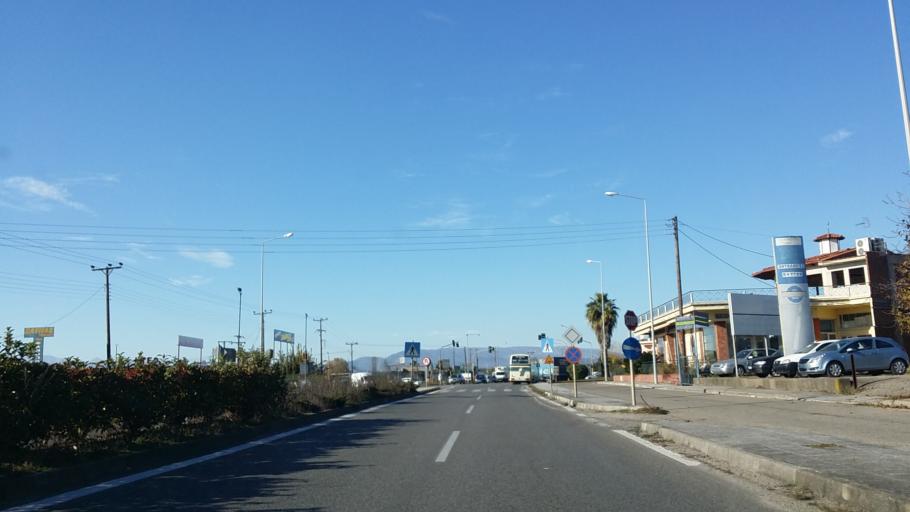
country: GR
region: West Greece
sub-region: Nomos Aitolias kai Akarnanias
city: Ayios Konstandinos
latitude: 38.6274
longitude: 21.3950
